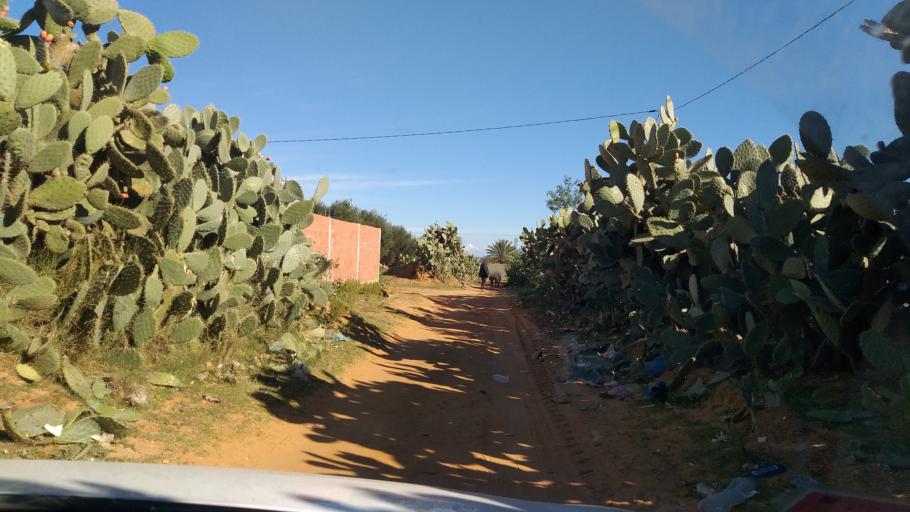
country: TN
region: Al Mahdiyah
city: El Jem
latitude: 35.2560
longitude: 10.6089
